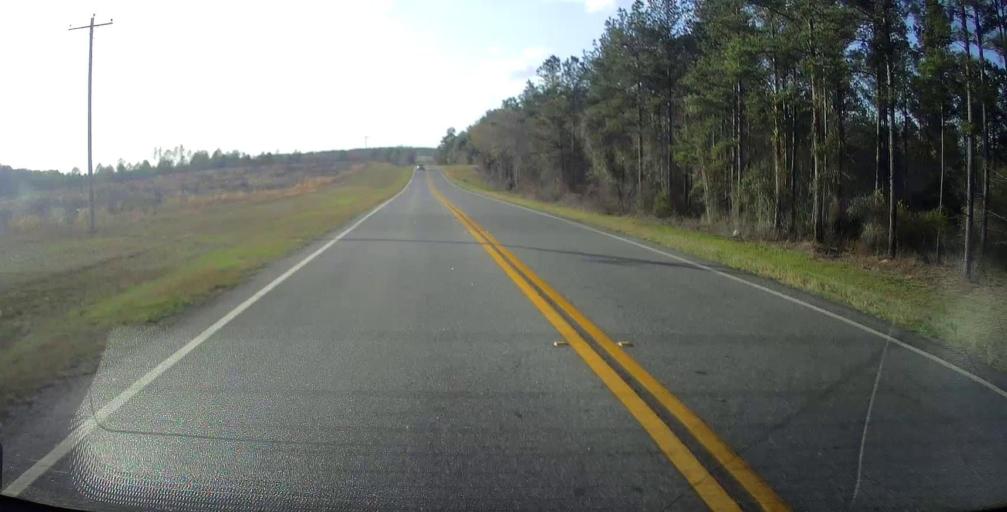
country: US
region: Georgia
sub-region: Tattnall County
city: Reidsville
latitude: 32.1282
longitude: -82.2130
